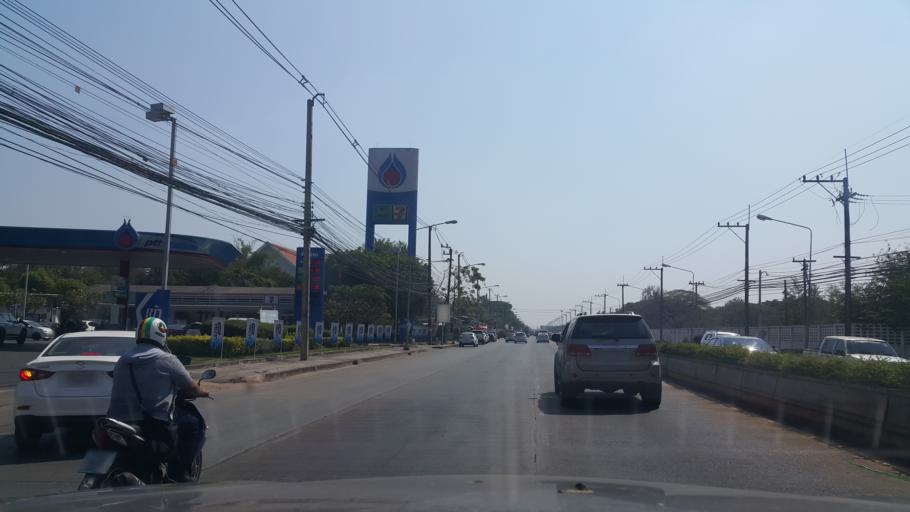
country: TH
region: Changwat Udon Thani
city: Udon Thani
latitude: 17.3860
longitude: 102.8031
